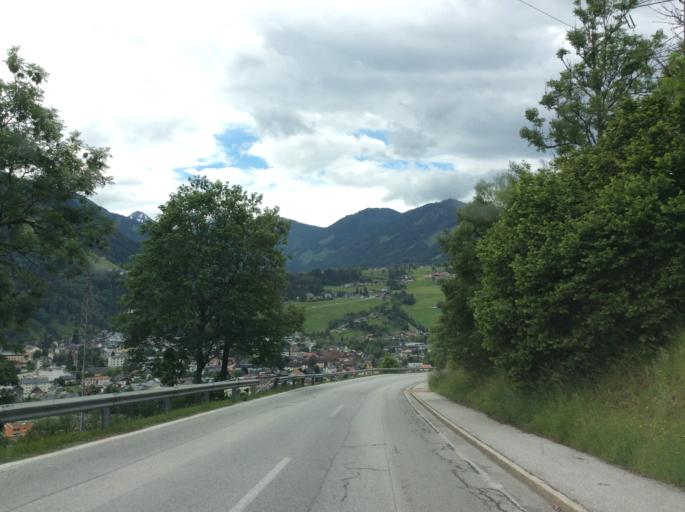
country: AT
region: Styria
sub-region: Politischer Bezirk Liezen
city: Schladming
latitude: 47.4014
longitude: 13.6922
